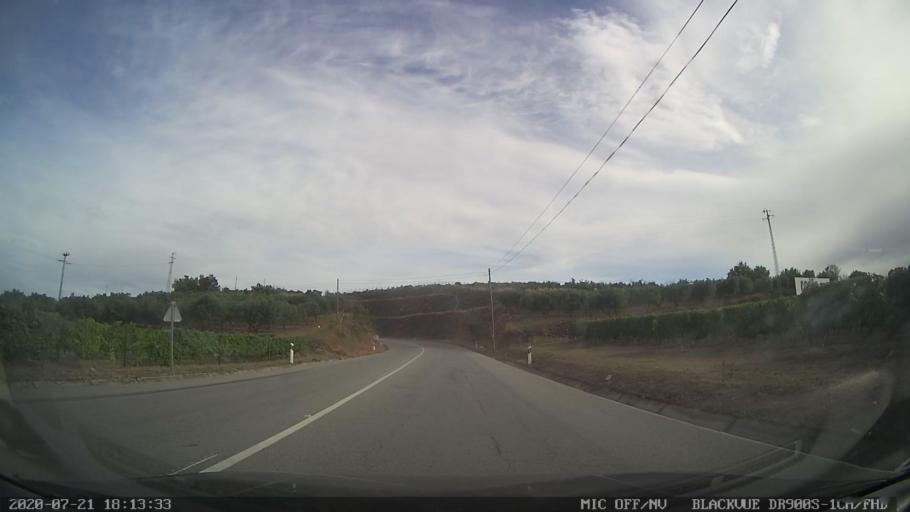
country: PT
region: Viseu
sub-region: Sao Joao da Pesqueira
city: Sao Joao da Pesqueira
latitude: 41.1296
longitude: -7.3981
